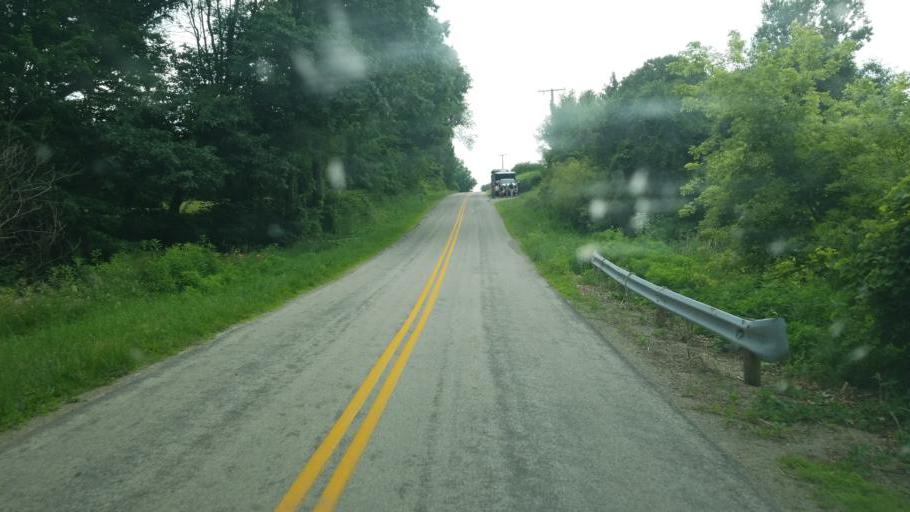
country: US
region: Ohio
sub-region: Wayne County
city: Shreve
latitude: 40.7775
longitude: -82.1357
